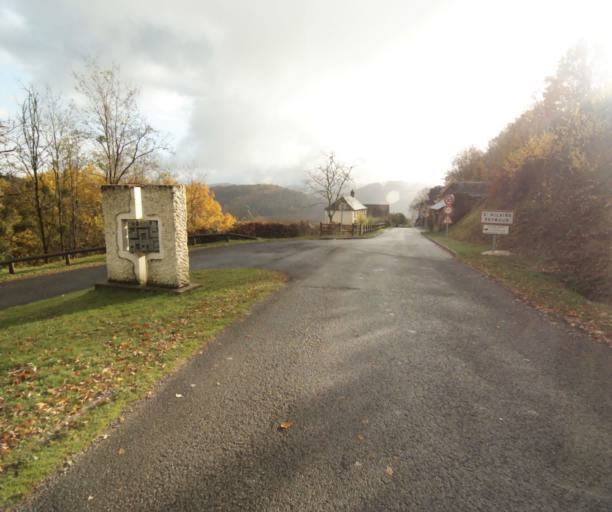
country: FR
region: Limousin
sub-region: Departement de la Correze
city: Cornil
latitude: 45.2147
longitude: 1.6463
